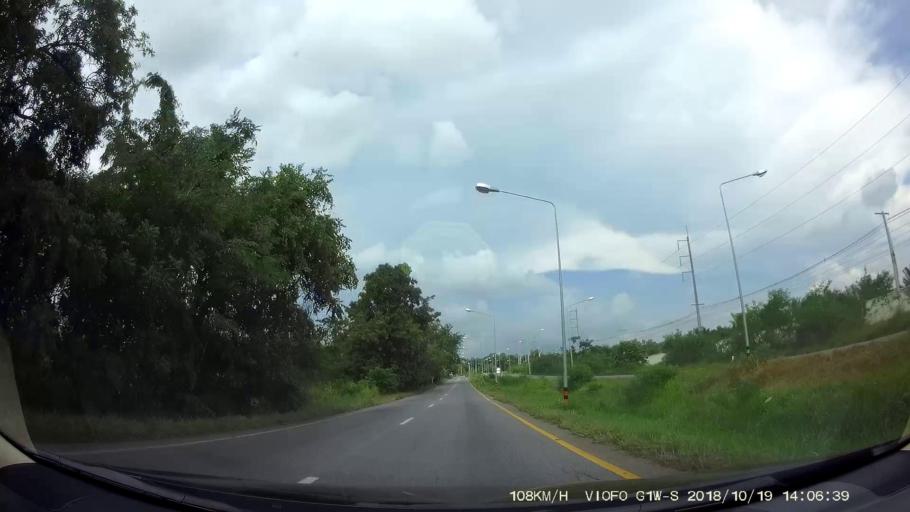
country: TH
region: Chaiyaphum
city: Chaiyaphum
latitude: 15.8894
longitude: 102.1071
